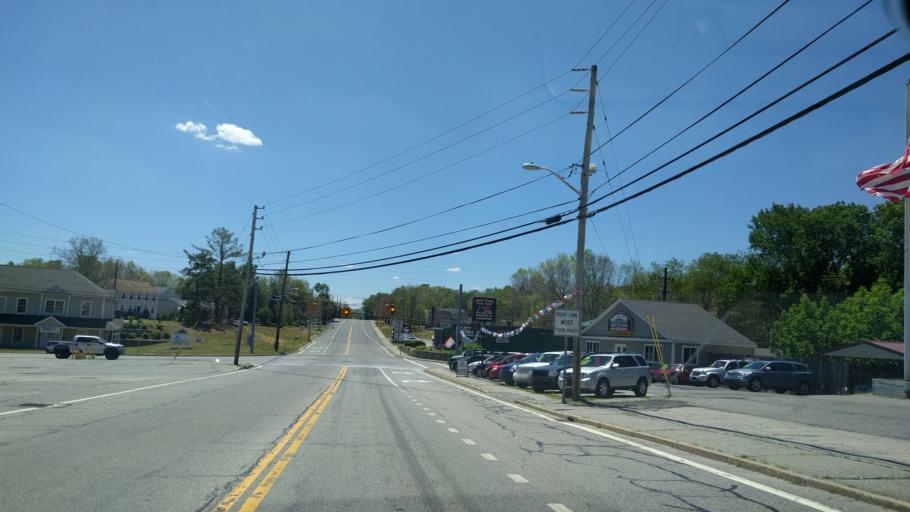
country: US
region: Massachusetts
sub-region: Worcester County
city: Millville
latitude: 41.9954
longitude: -71.5982
